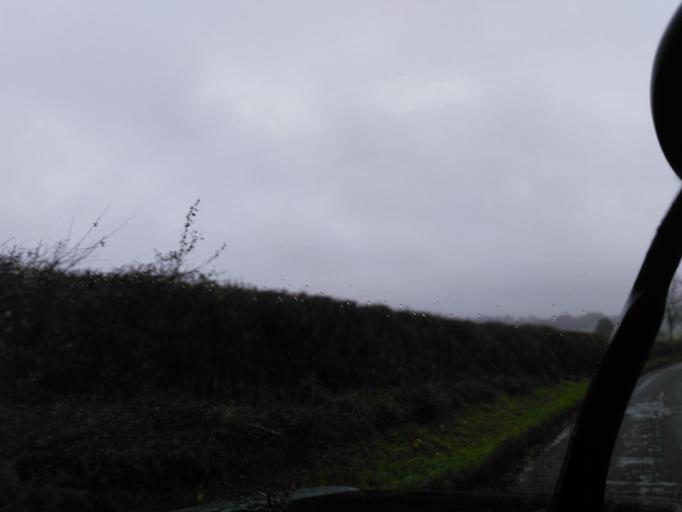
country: GB
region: England
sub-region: Bath and North East Somerset
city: Hinton Charterhouse
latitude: 51.3205
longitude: -2.3455
